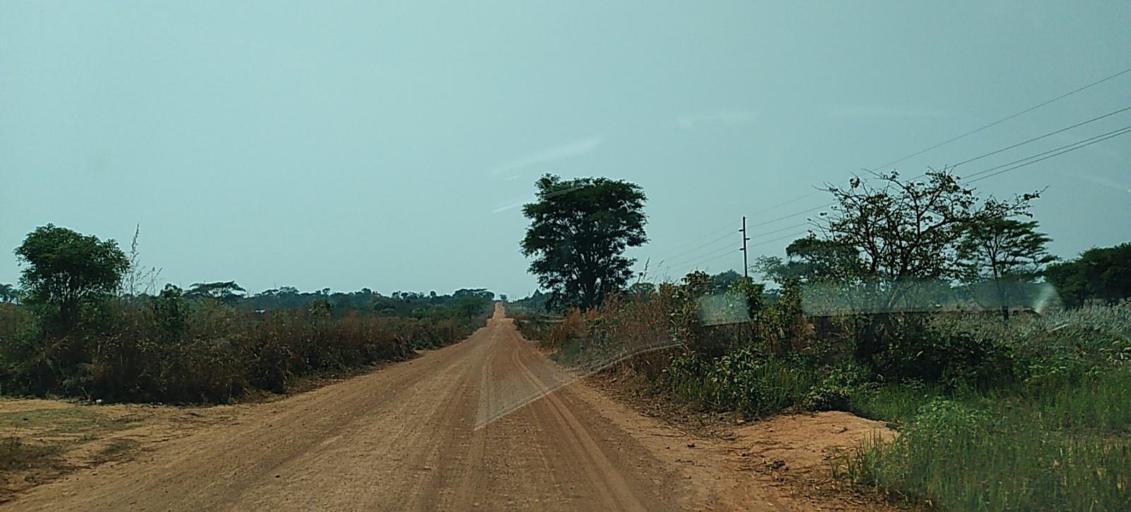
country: ZM
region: North-Western
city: Kansanshi
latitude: -12.0055
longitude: 26.5679
